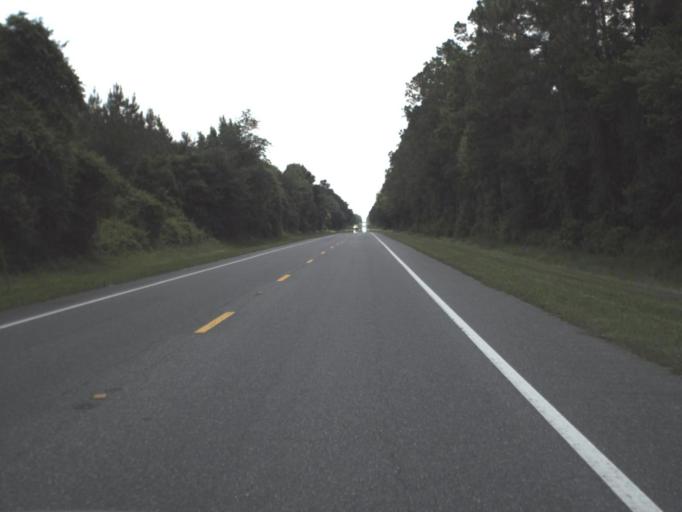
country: US
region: Florida
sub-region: Columbia County
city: Watertown
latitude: 30.1311
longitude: -82.5246
